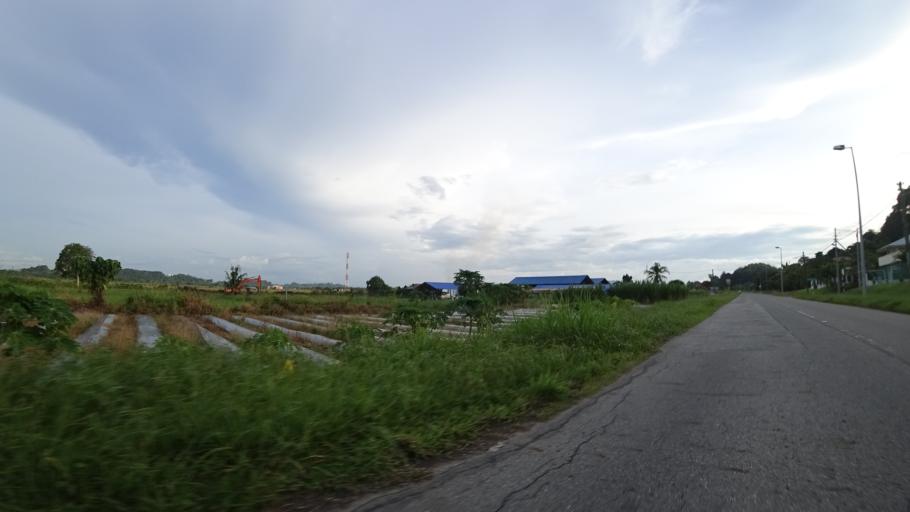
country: BN
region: Brunei and Muara
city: Bandar Seri Begawan
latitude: 4.8372
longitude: 114.8207
